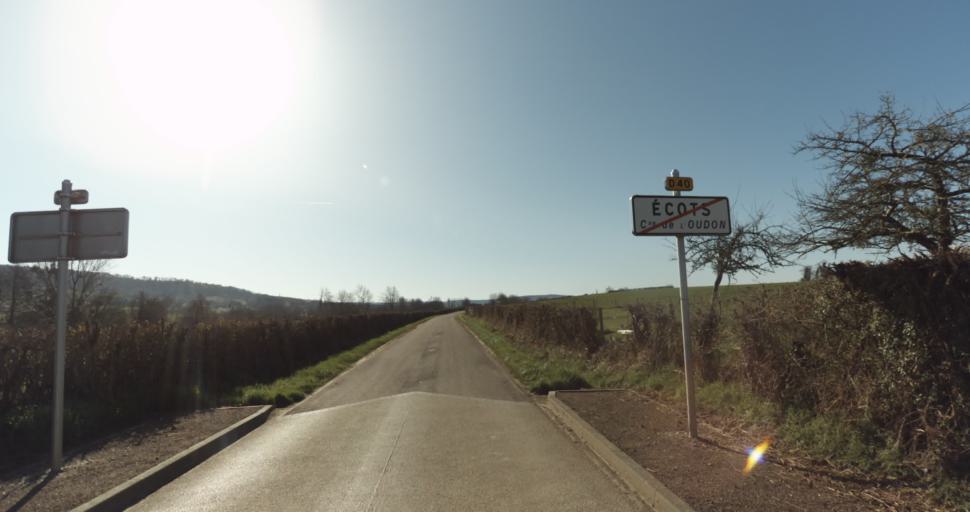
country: FR
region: Lower Normandy
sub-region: Departement du Calvados
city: Saint-Pierre-sur-Dives
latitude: 48.9864
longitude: 0.0304
